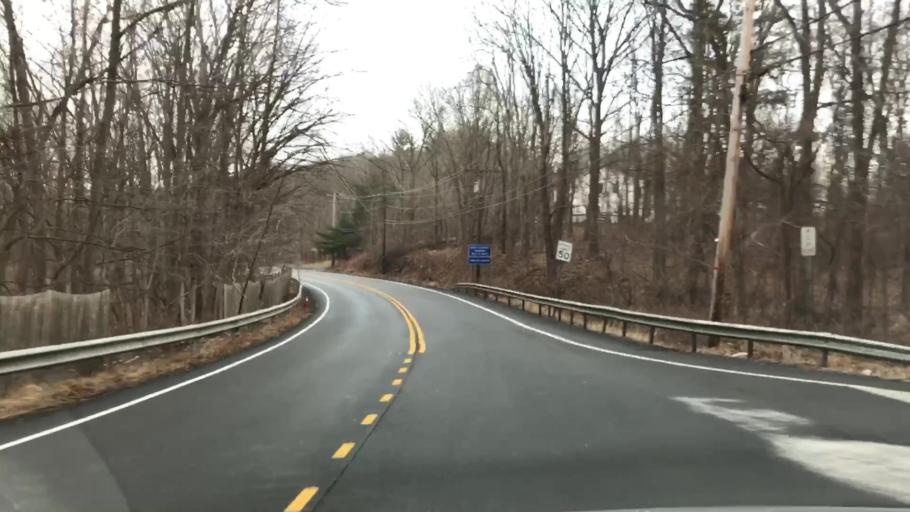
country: US
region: New York
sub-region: Rockland County
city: Wesley Hills
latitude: 41.1711
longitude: -74.0849
